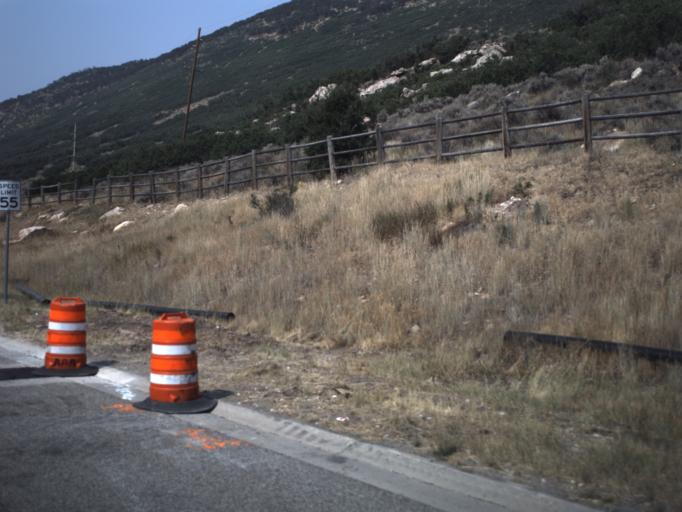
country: US
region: Utah
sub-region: Summit County
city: Snyderville
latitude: 40.6763
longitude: -111.5218
